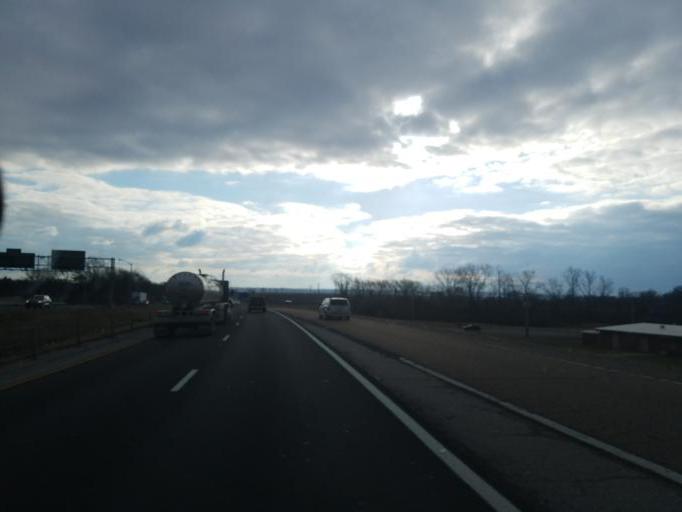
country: US
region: Illinois
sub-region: Madison County
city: Mitchell
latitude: 38.7578
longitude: -90.0885
